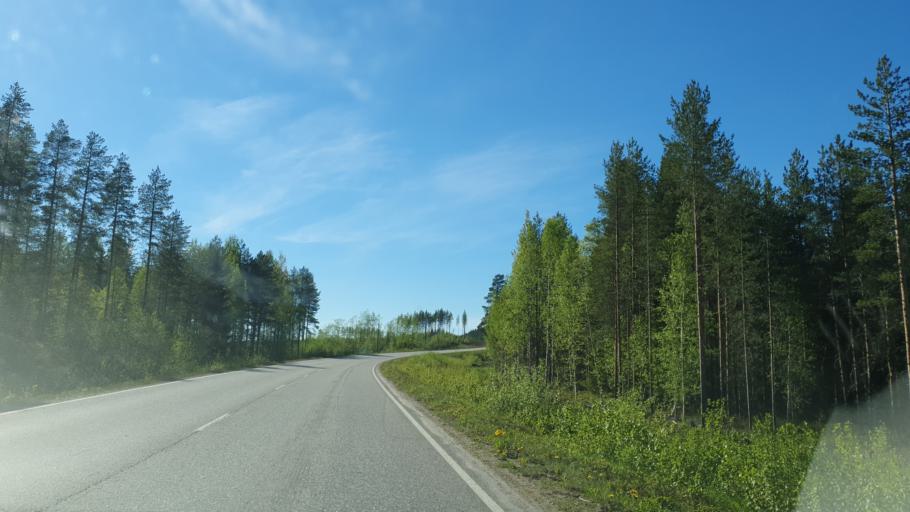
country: FI
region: Kainuu
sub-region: Kehys-Kainuu
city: Kuhmo
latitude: 64.1449
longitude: 29.4267
